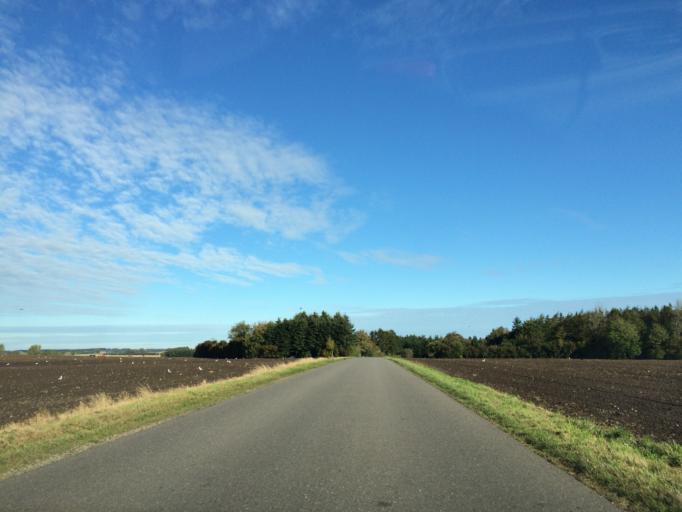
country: DK
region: Central Jutland
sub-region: Favrskov Kommune
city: Ulstrup
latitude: 56.2928
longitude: 9.7676
